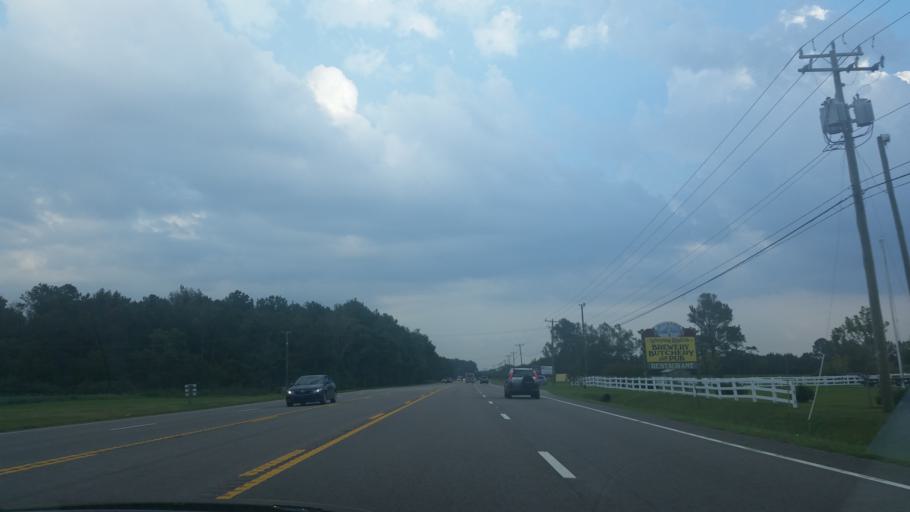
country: US
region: North Carolina
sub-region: Dare County
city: Southern Shores
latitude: 36.2206
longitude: -75.8695
